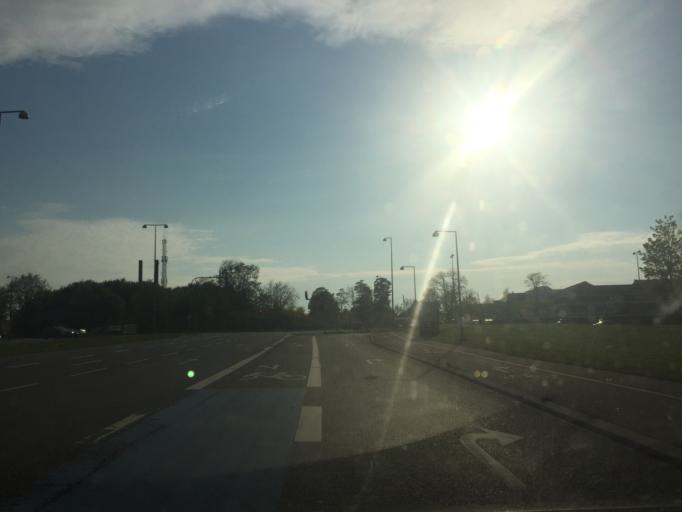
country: DK
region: Capital Region
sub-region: Hoje-Taastrup Kommune
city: Taastrup
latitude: 55.6569
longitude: 12.2845
